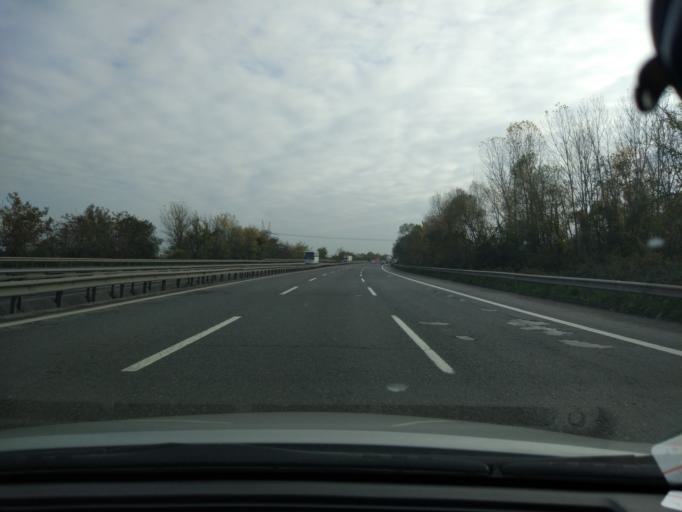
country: TR
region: Sakarya
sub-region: Merkez
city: Sapanca
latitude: 40.7124
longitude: 30.3292
